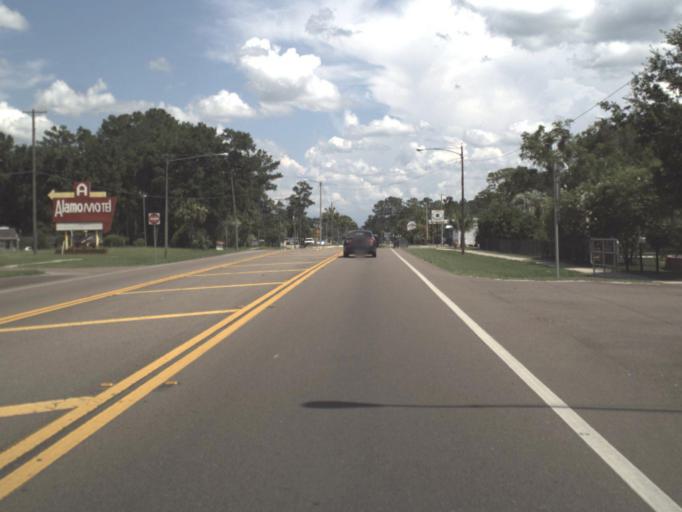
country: US
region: Florida
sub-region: Alachua County
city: High Springs
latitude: 29.8376
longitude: -82.6012
